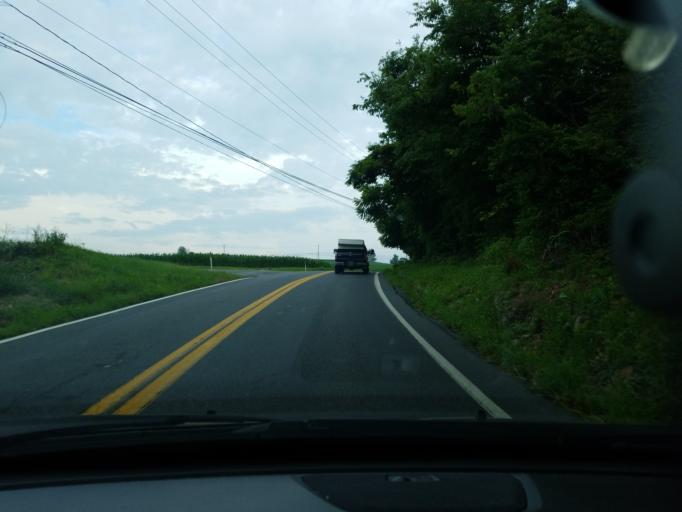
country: US
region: Pennsylvania
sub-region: Dauphin County
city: Middletown
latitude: 40.2041
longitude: -76.6780
